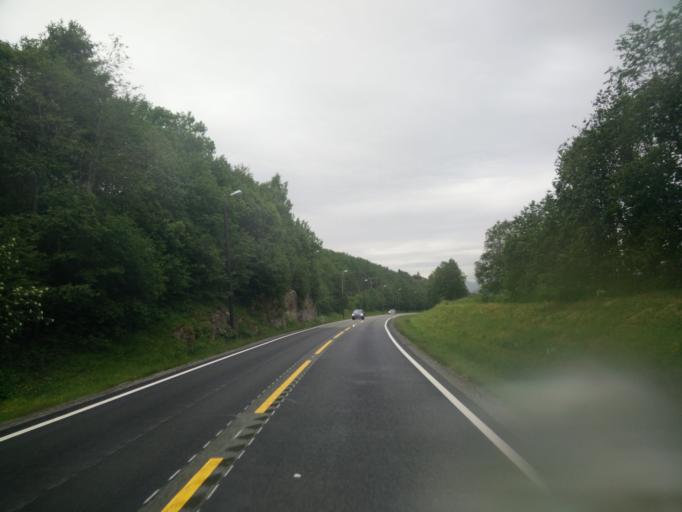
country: NO
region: Sor-Trondelag
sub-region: Orkdal
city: Orkanger
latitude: 63.2811
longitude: 9.8460
